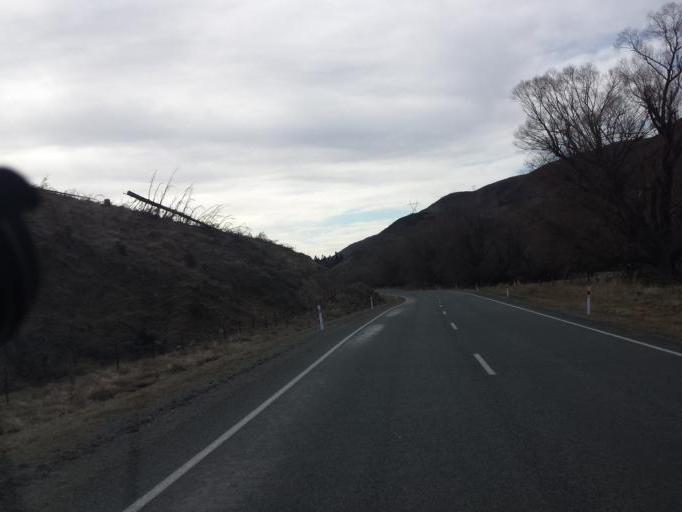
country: NZ
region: Canterbury
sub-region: Timaru District
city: Pleasant Point
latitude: -44.0701
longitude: 170.6682
